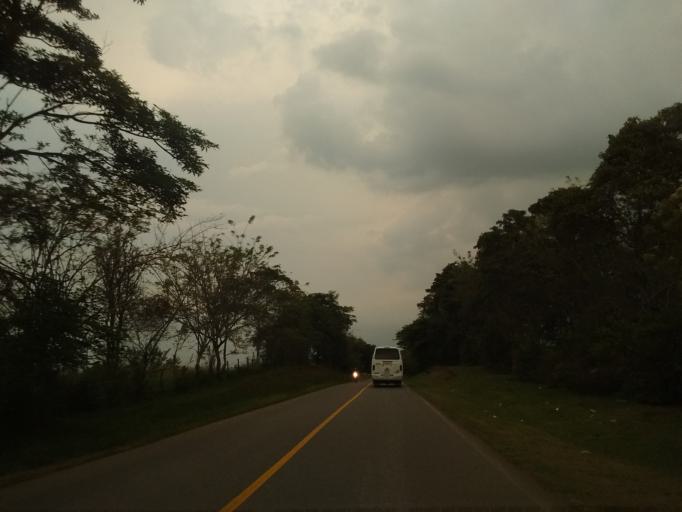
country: CO
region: Cauca
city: Caloto
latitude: 3.0539
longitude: -76.3774
